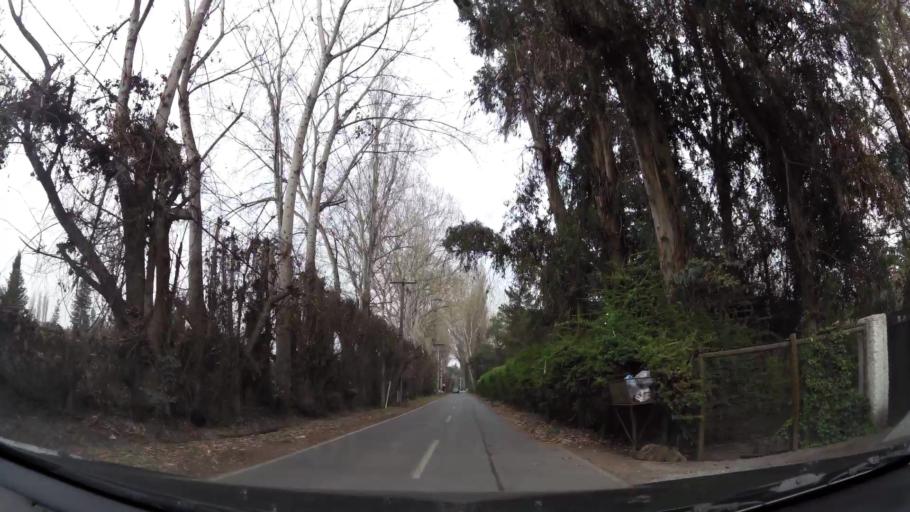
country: CL
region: Santiago Metropolitan
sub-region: Provincia de Chacabuco
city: Chicureo Abajo
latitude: -33.2684
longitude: -70.7094
